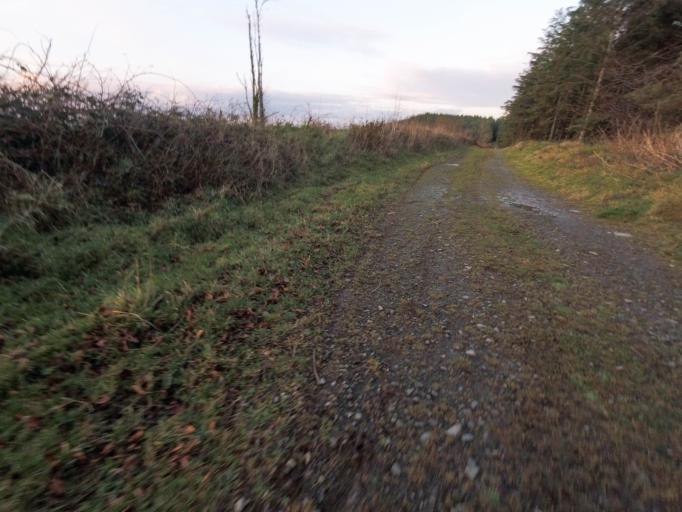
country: IE
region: Munster
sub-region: Waterford
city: Portlaw
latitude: 52.3097
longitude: -7.3479
